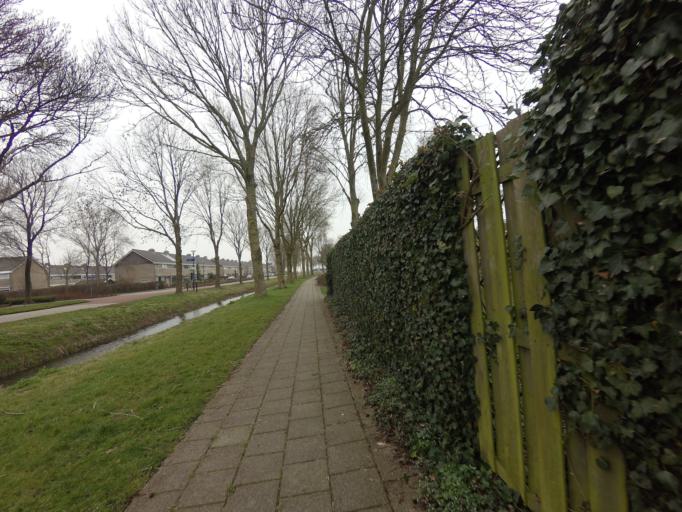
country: NL
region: Friesland
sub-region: Gemeente Franekeradeel
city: Franeker
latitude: 53.1905
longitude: 5.5616
